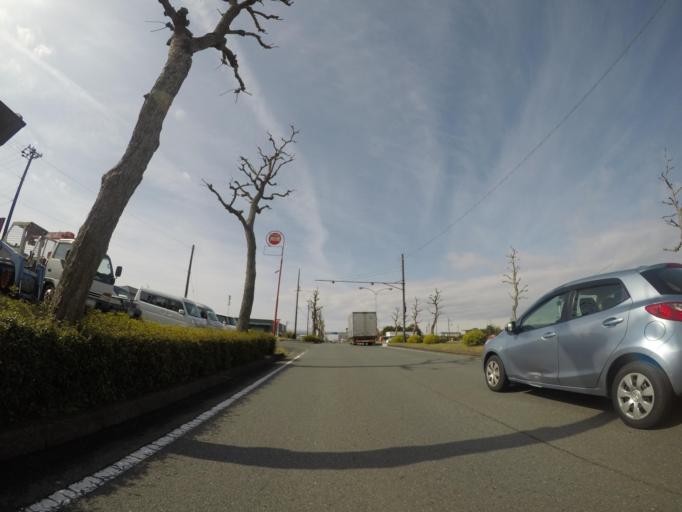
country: JP
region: Shizuoka
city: Hamamatsu
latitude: 34.7716
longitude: 137.6918
